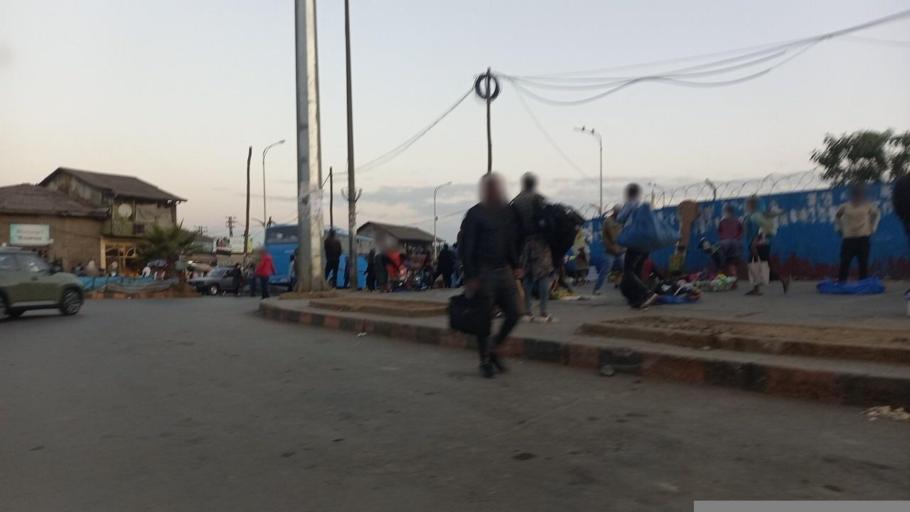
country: ET
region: Adis Abeba
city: Addis Ababa
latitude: 9.0354
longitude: 38.7524
